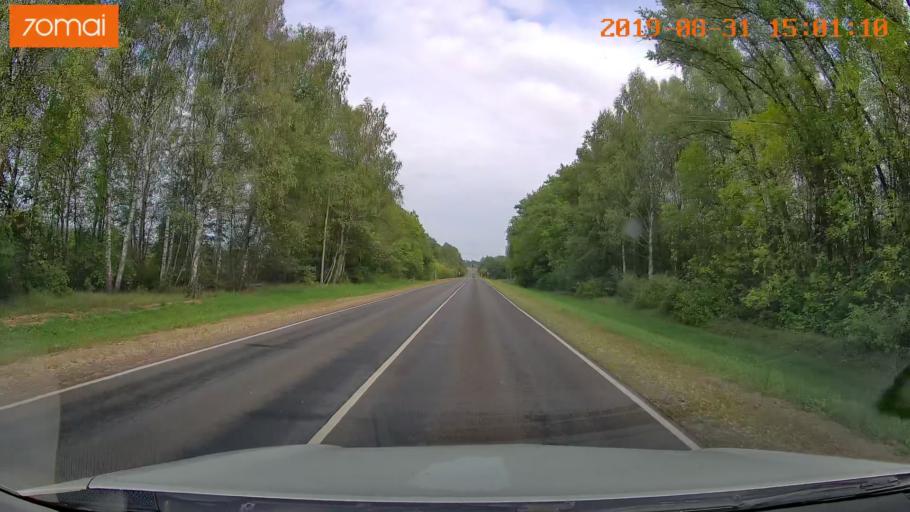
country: RU
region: Kaluga
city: Spas-Demensk
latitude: 54.3374
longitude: 34.0498
